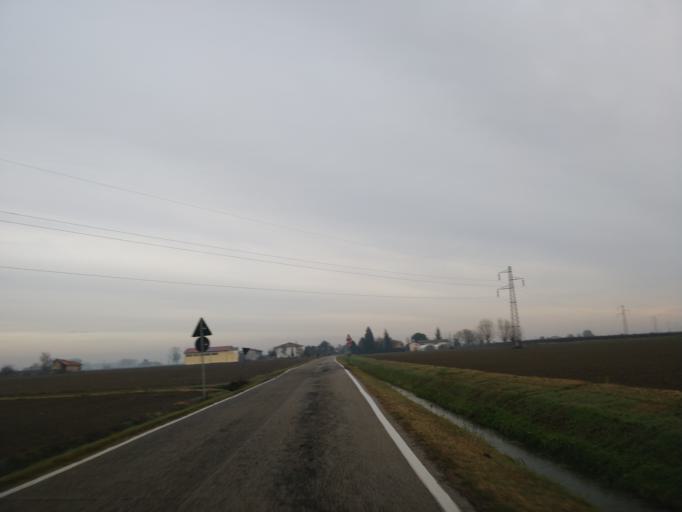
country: IT
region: Emilia-Romagna
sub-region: Provincia di Ferrara
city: Dosso
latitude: 44.7728
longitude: 11.3281
